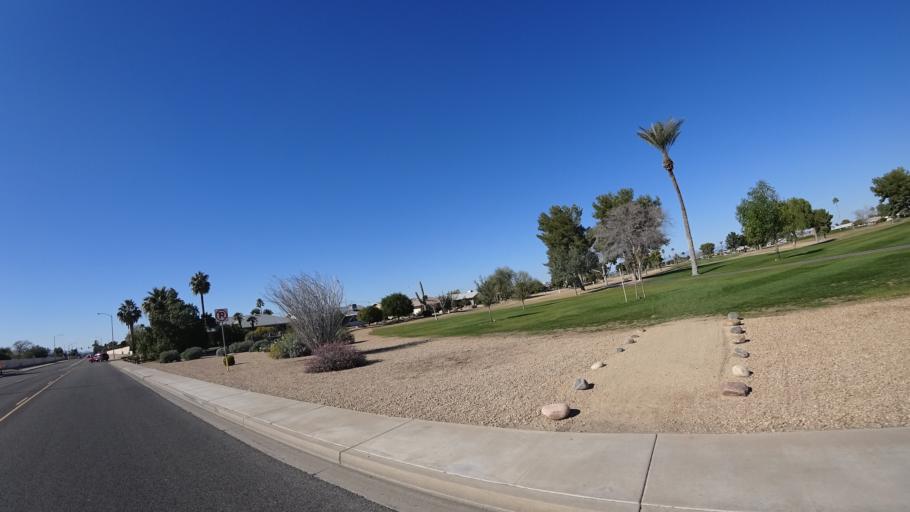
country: US
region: Arizona
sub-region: Maricopa County
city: Surprise
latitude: 33.6525
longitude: -112.2861
